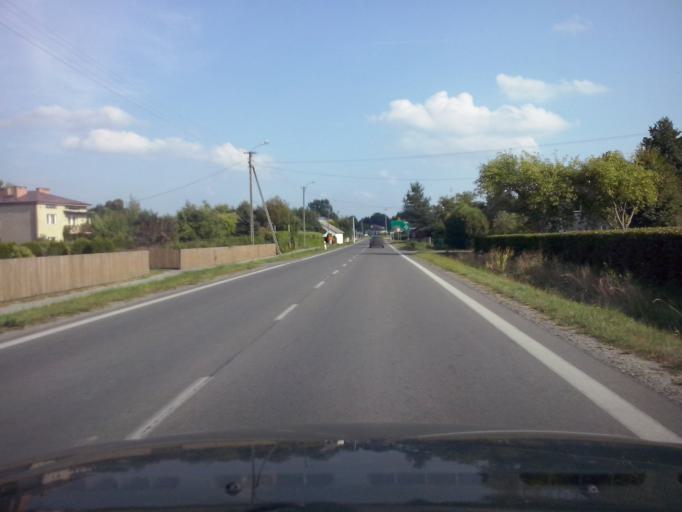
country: PL
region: Subcarpathian Voivodeship
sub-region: Powiat kolbuszowski
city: Kolbuszowa
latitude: 50.2510
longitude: 21.7642
